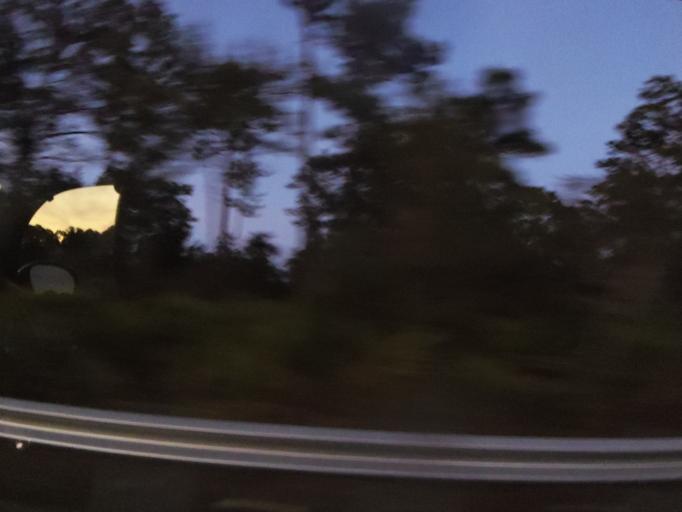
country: US
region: Florida
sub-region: Saint Johns County
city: Saint Augustine South
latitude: 29.8296
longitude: -81.3546
